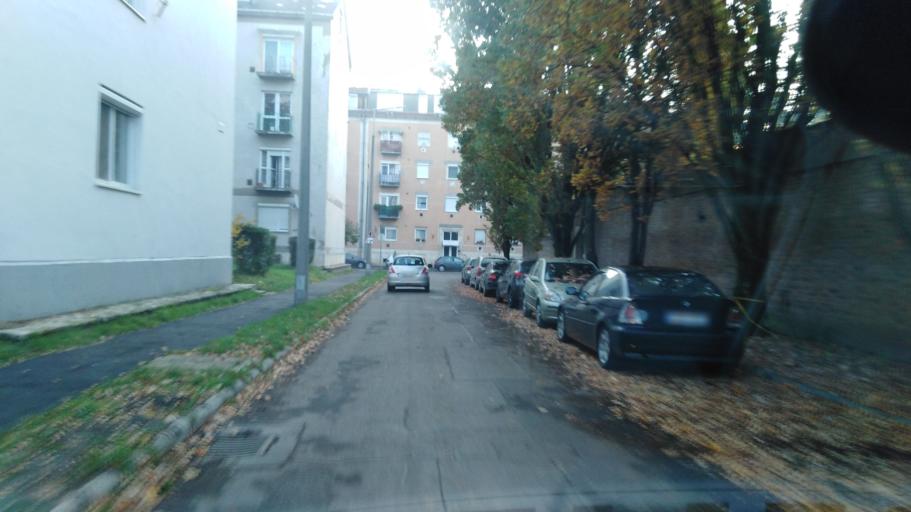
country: HU
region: Nograd
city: Salgotarjan
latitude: 48.0991
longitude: 19.8034
